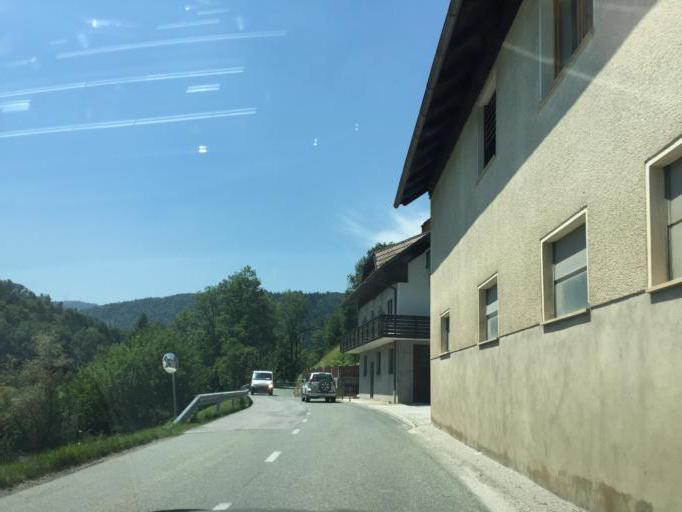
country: SI
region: Gorenja Vas-Poljane
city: Gorenja Vas
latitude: 46.1069
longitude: 14.1290
